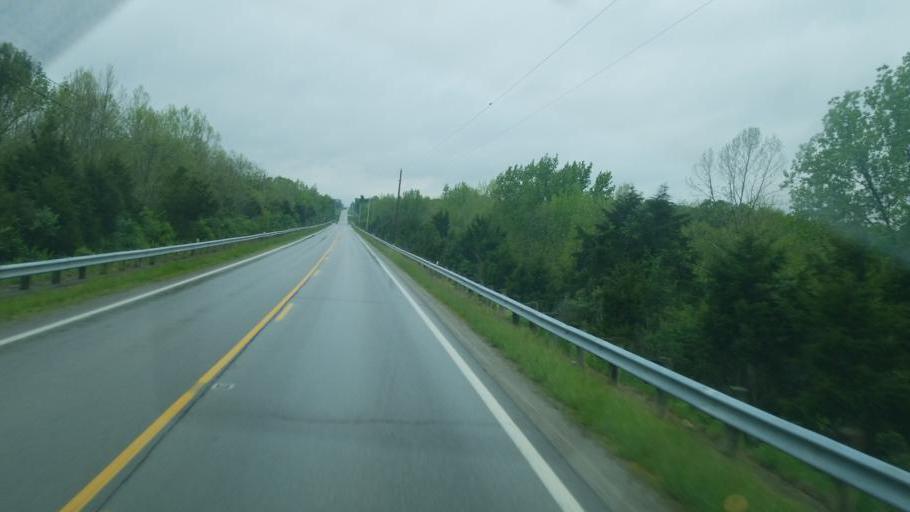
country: US
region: Ohio
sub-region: Highland County
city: Greenfield
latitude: 39.2930
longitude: -83.4537
